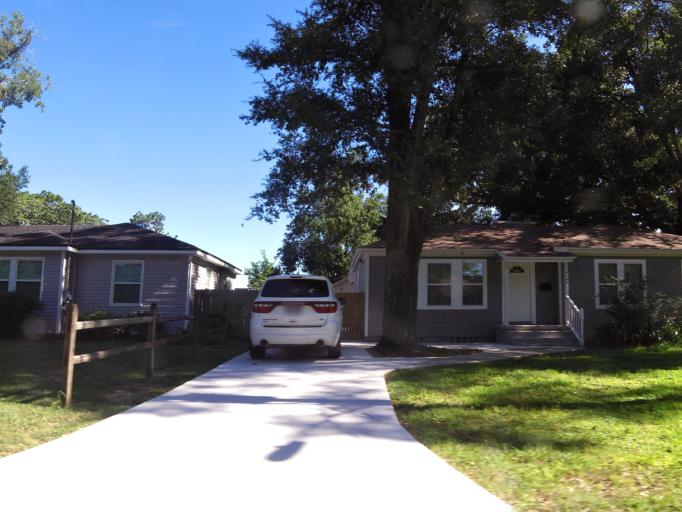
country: US
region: Florida
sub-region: Duval County
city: Jacksonville
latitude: 30.2755
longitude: -81.7251
